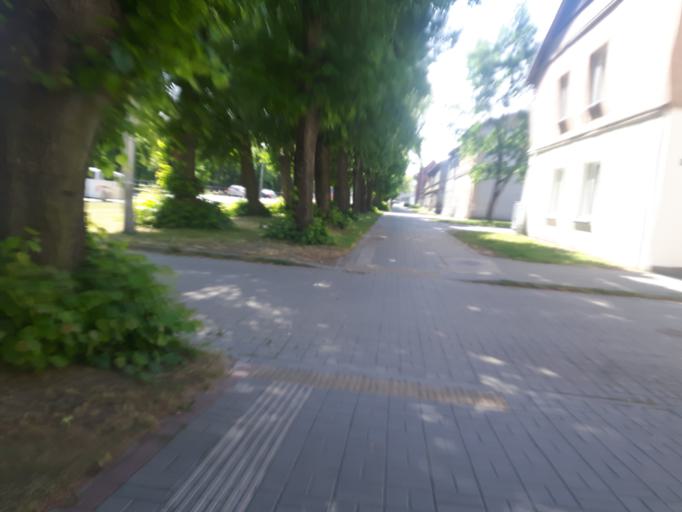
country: LV
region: Liepaja
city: Liepaja
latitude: 56.5225
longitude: 21.0230
